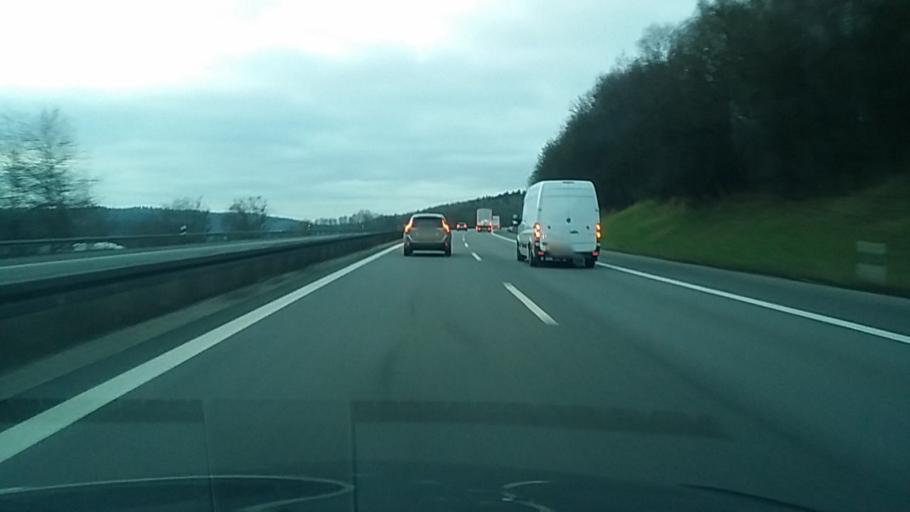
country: DE
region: Bavaria
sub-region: Upper Palatinate
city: Pilsach
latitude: 49.3453
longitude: 11.4434
